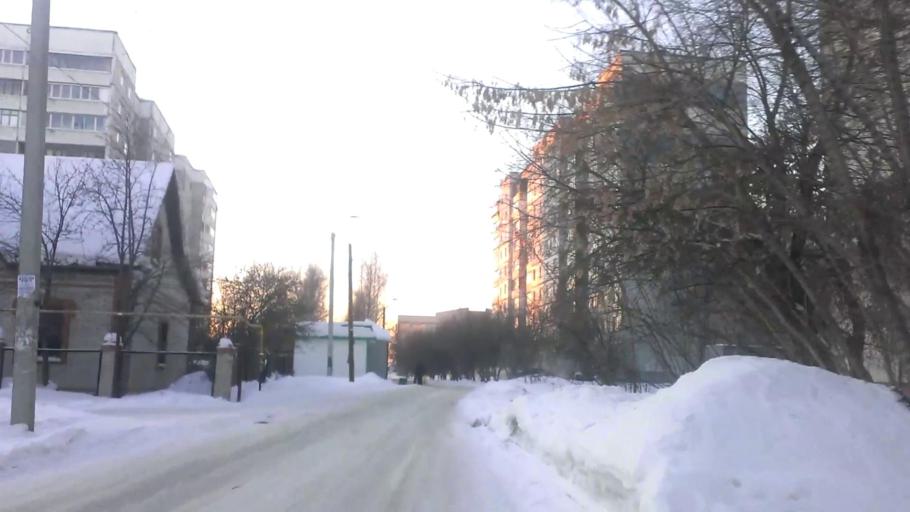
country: RU
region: Altai Krai
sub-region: Gorod Barnaulskiy
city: Barnaul
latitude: 53.3541
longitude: 83.7014
